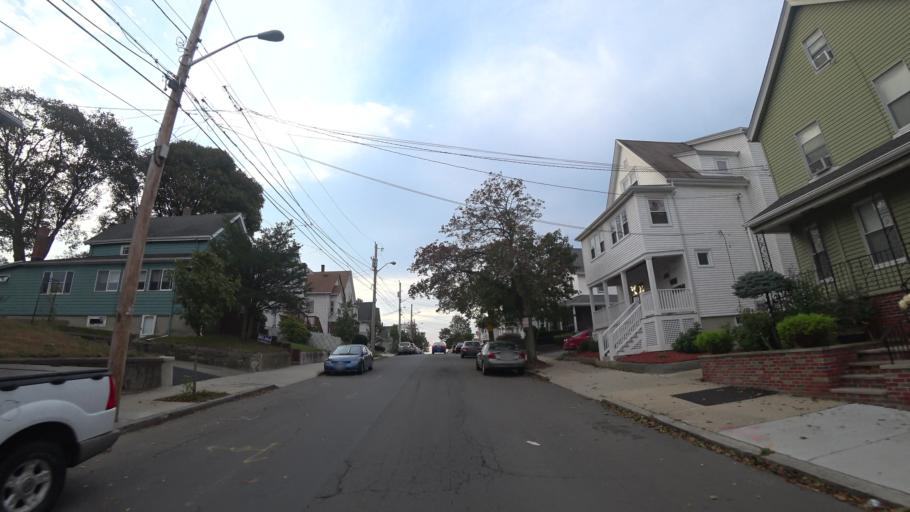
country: US
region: Massachusetts
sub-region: Middlesex County
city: Everett
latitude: 42.4114
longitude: -71.0501
